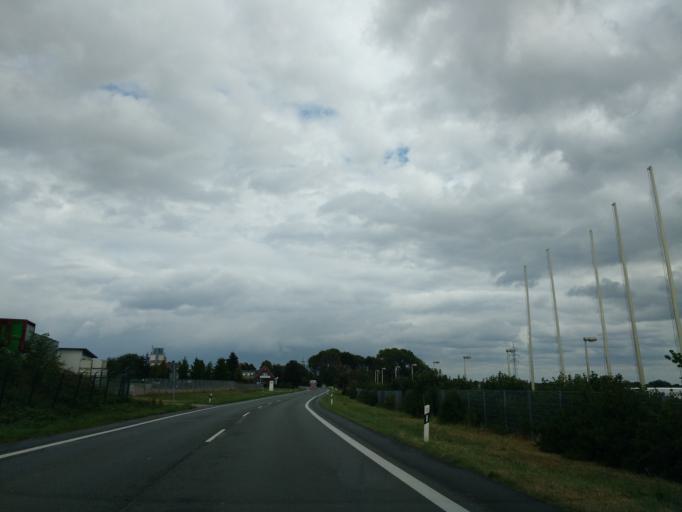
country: DE
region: Lower Saxony
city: Bad Laer
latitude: 52.1014
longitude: 8.1069
